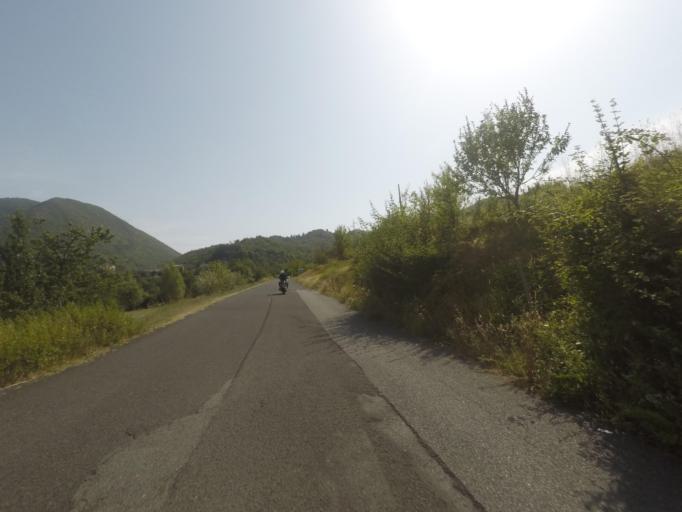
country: IT
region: Tuscany
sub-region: Provincia di Massa-Carrara
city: Fivizzano
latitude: 44.1727
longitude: 10.1103
